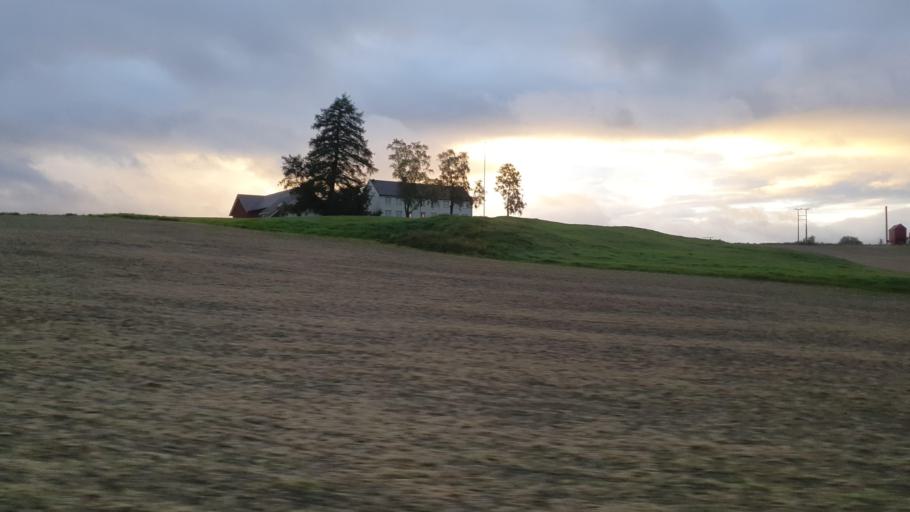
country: NO
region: Nord-Trondelag
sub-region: Levanger
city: Skogn
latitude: 63.6826
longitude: 11.1745
